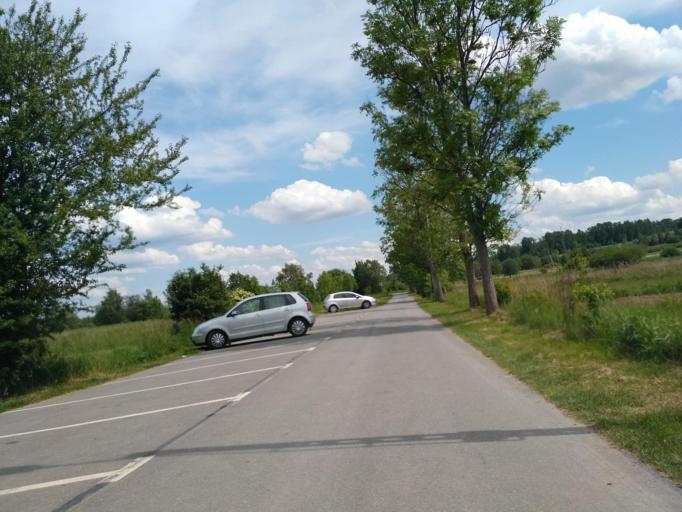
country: PL
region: Subcarpathian Voivodeship
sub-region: Powiat krosnienski
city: Odrzykon
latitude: 49.7175
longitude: 21.7576
